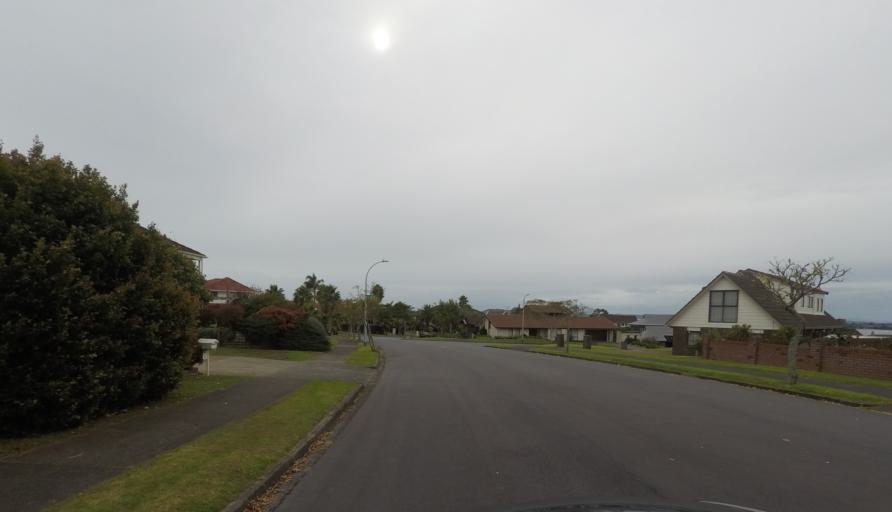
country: NZ
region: Auckland
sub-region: Auckland
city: Pakuranga
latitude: -36.8962
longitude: 174.9479
